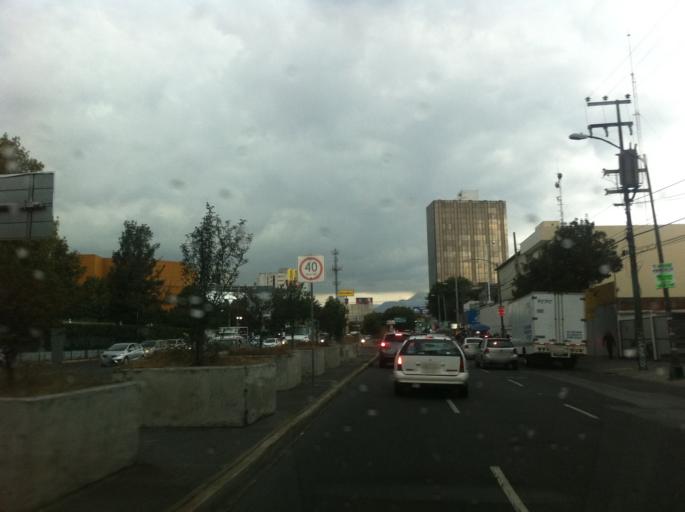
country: MX
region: Mexico City
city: Coyoacan
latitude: 19.3624
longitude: -99.1704
